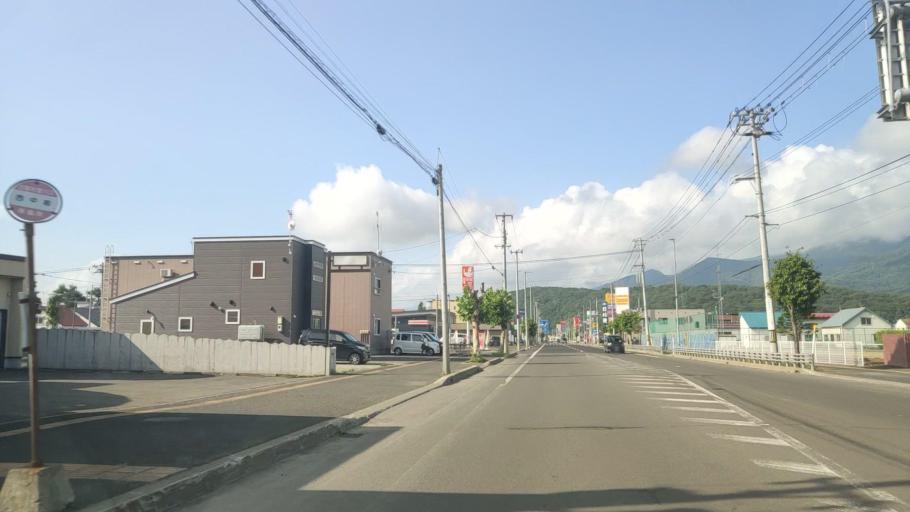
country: JP
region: Hokkaido
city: Shimo-furano
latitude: 43.3483
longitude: 142.3847
